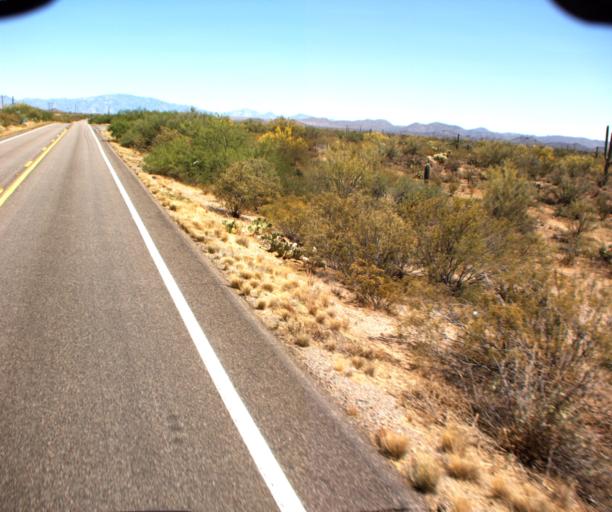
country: US
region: Arizona
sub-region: Pima County
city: Catalina
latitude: 32.6910
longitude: -111.0817
